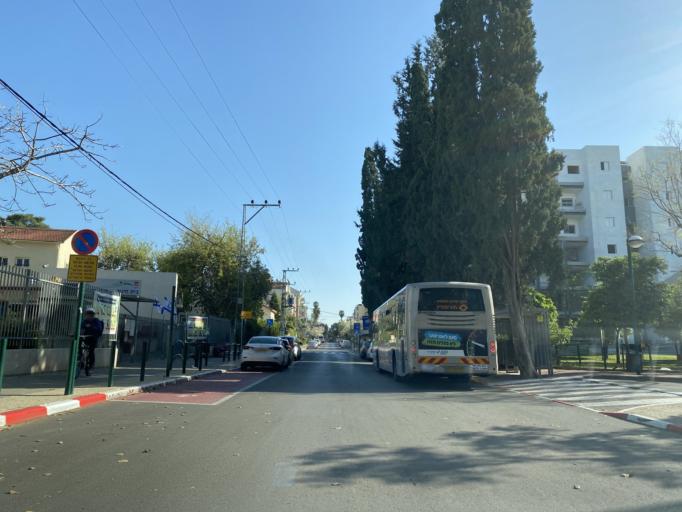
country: IL
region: Central District
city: Kfar Saba
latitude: 32.1782
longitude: 34.9183
